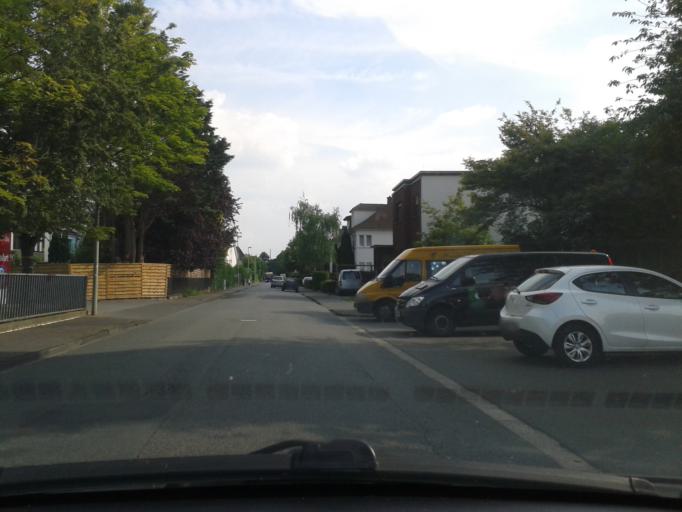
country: DE
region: North Rhine-Westphalia
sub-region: Regierungsbezirk Detmold
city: Paderborn
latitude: 51.7151
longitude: 8.7296
